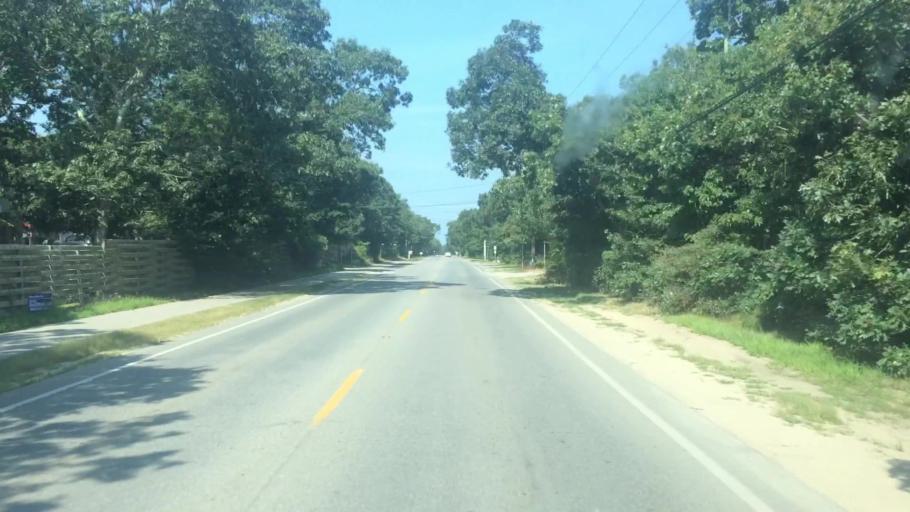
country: US
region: Massachusetts
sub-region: Dukes County
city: Edgartown
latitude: 41.4045
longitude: -70.5590
